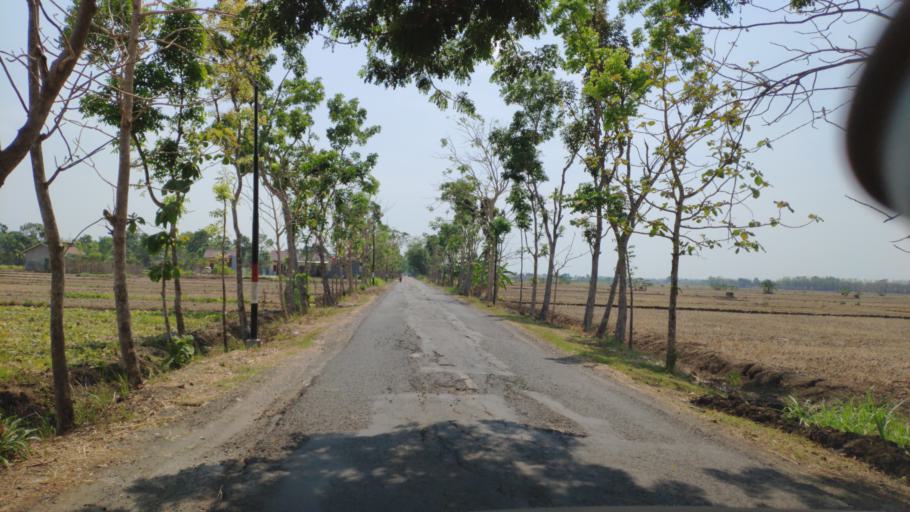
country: ID
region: Central Java
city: Kedungjenar
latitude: -6.9803
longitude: 111.4267
